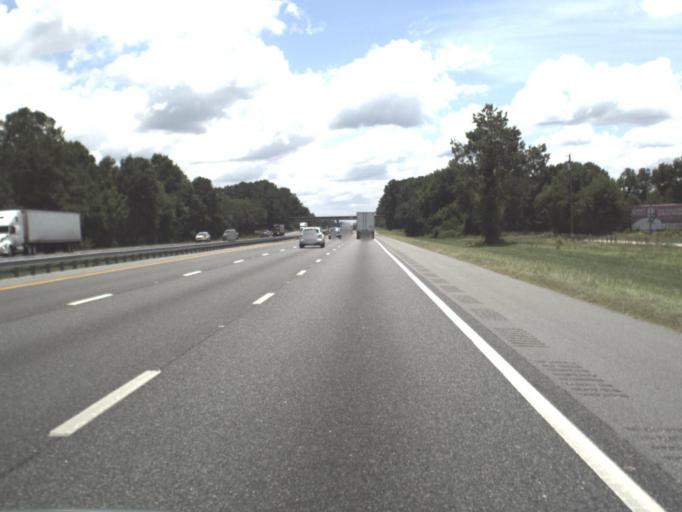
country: US
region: Florida
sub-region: Columbia County
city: Lake City
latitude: 30.0314
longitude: -82.6142
